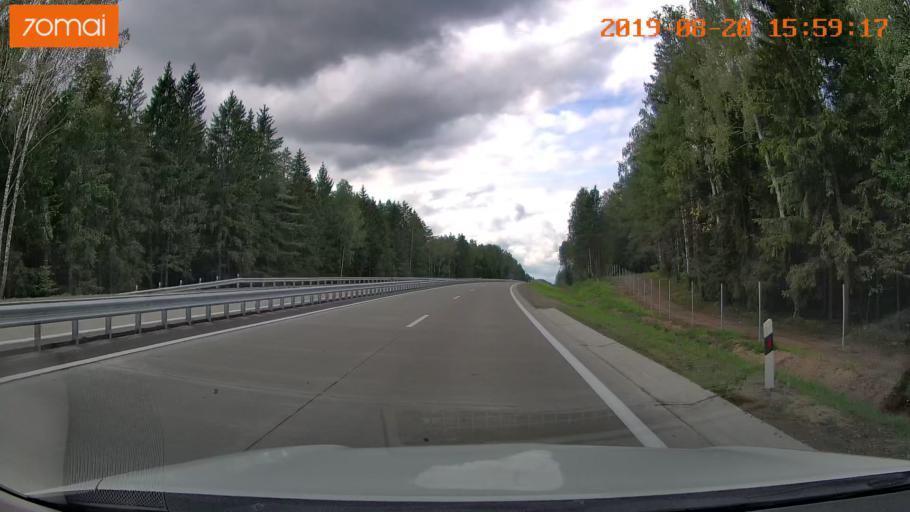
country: BY
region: Minsk
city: Korolev Stan
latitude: 54.0370
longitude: 27.8192
